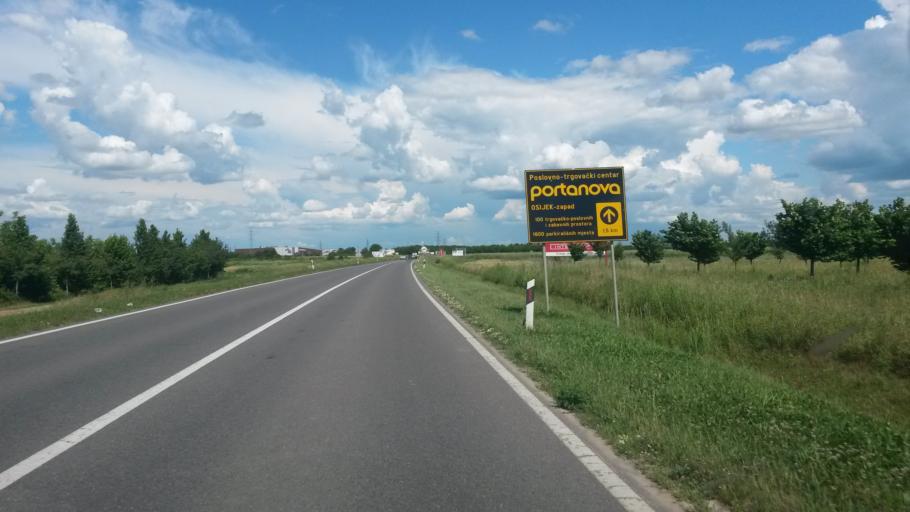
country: HR
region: Osjecko-Baranjska
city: Visnjevac
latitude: 45.5477
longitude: 18.6190
